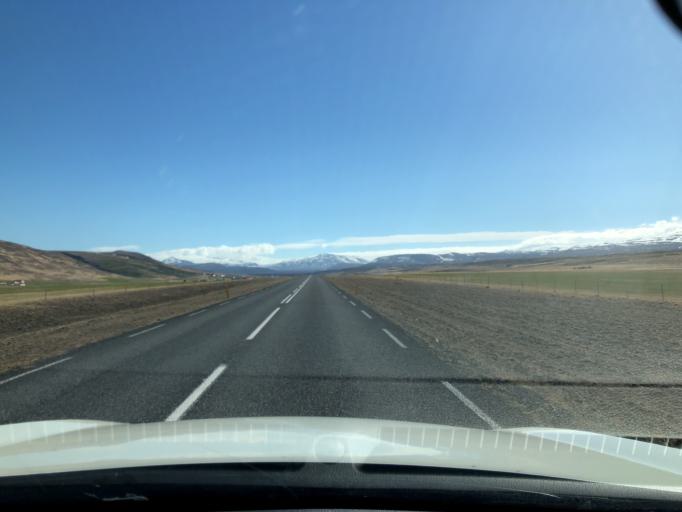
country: IS
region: South
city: Hveragerdi
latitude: 64.7027
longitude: -21.1409
